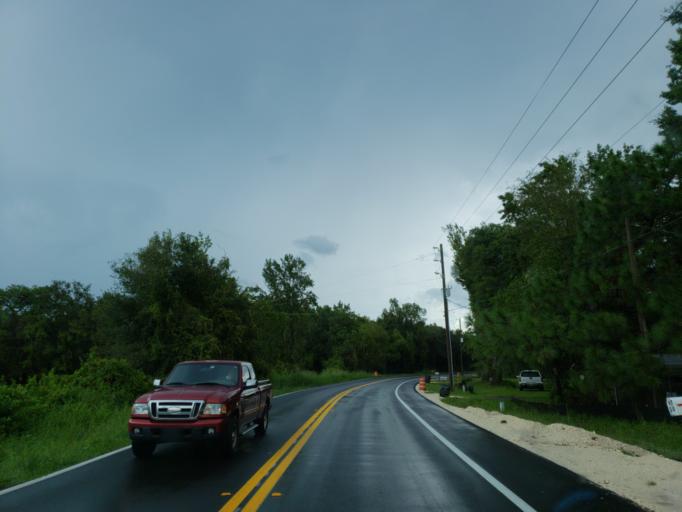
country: US
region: Florida
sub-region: Pasco County
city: Land O' Lakes
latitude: 28.2998
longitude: -82.4317
